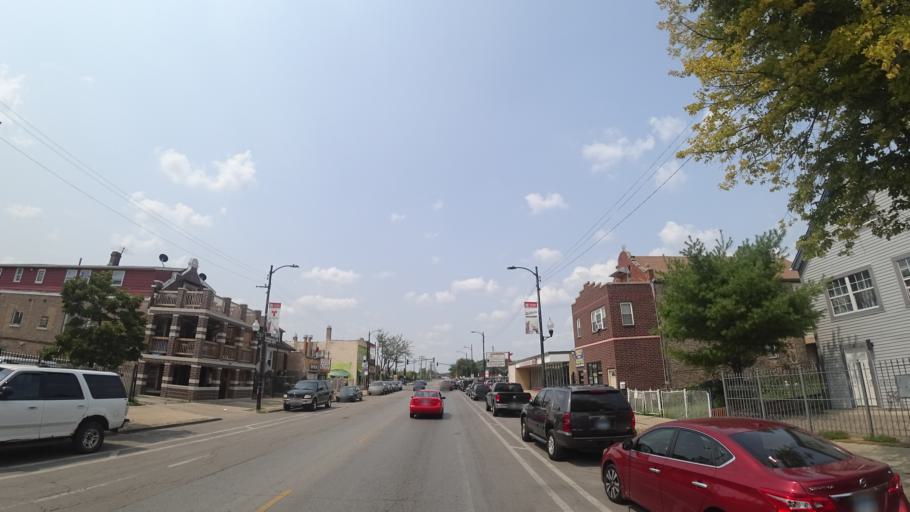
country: US
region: Illinois
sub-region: Cook County
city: Cicero
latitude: 41.8441
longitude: -87.7331
